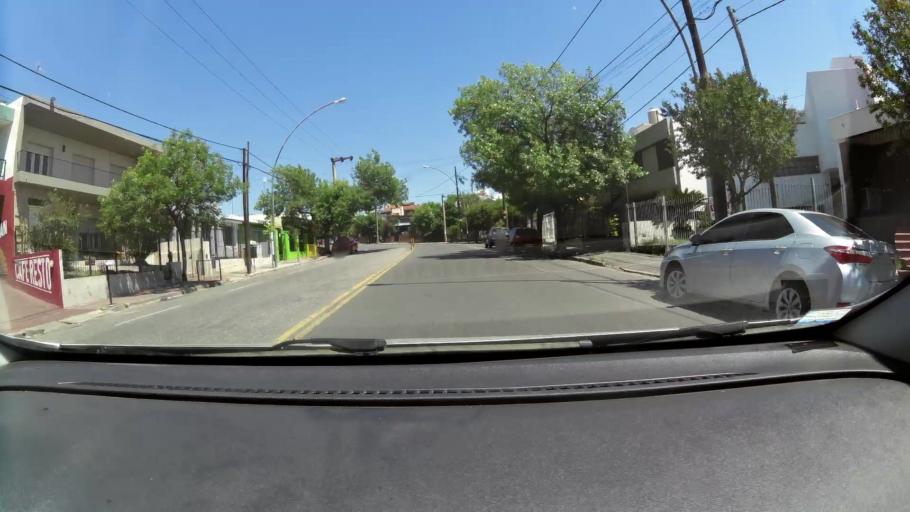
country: AR
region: Cordoba
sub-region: Departamento de Capital
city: Cordoba
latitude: -31.4163
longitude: -64.2048
